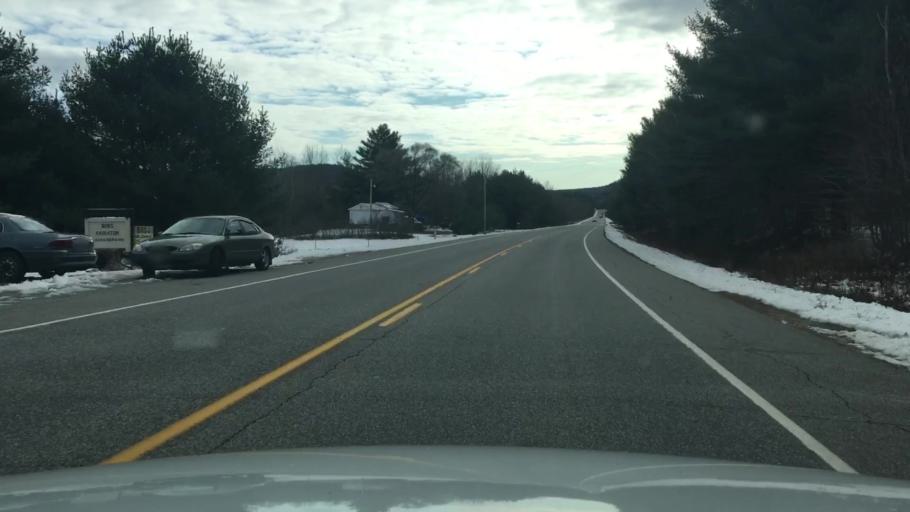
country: US
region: Maine
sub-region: Oxford County
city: Canton
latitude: 44.4322
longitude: -70.3030
